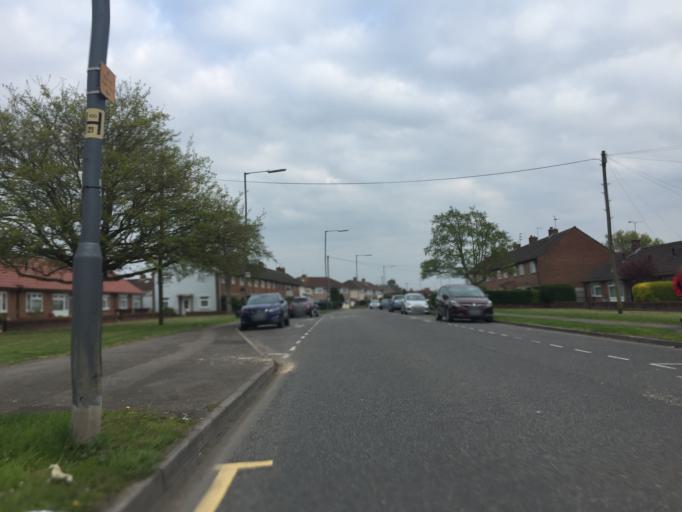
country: GB
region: England
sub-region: South Gloucestershire
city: Stoke Gifford
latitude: 51.5142
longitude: -2.5692
